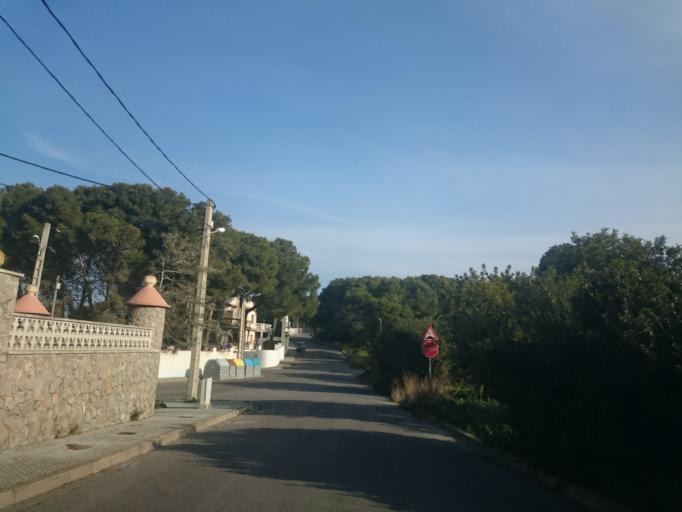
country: ES
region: Catalonia
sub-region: Provincia de Barcelona
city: Vilanova i la Geltru
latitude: 41.2302
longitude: 1.7598
